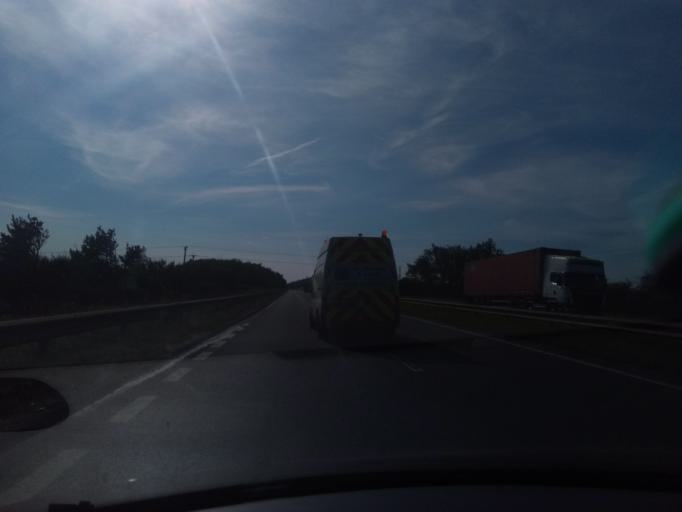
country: GB
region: England
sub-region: County Durham
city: Seaham
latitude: 54.8319
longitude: -1.3739
